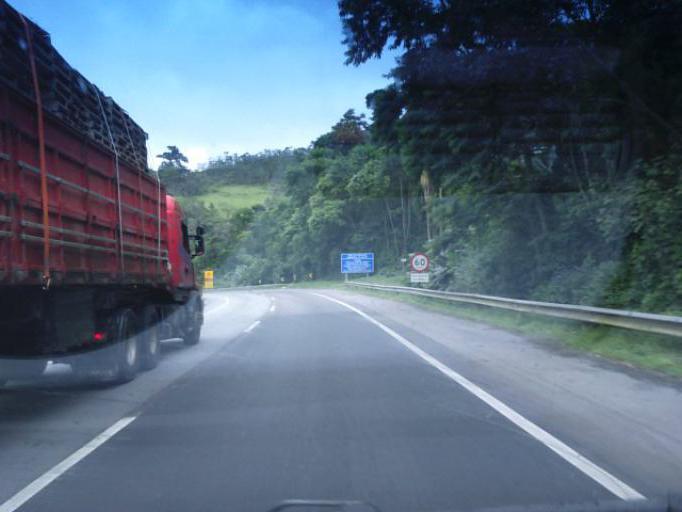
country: BR
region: Sao Paulo
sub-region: Cajati
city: Cajati
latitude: -24.8655
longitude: -48.2114
